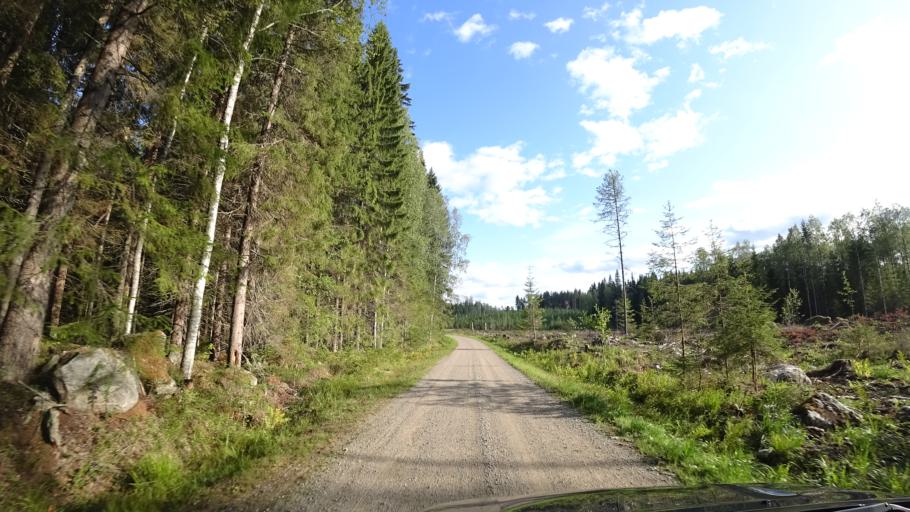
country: FI
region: Paijanne Tavastia
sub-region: Lahti
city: Auttoinen
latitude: 61.2176
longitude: 25.1512
